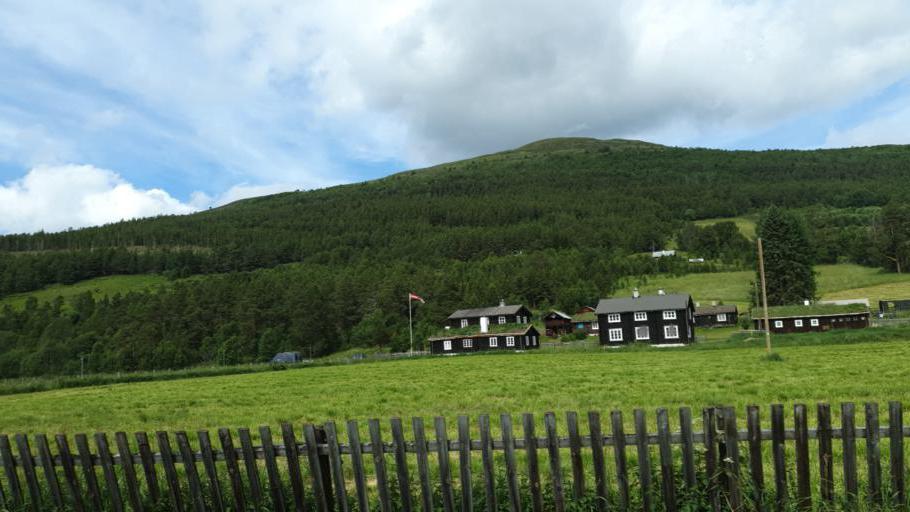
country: NO
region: Oppland
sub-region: Vaga
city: Vagamo
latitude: 61.7278
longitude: 9.0689
